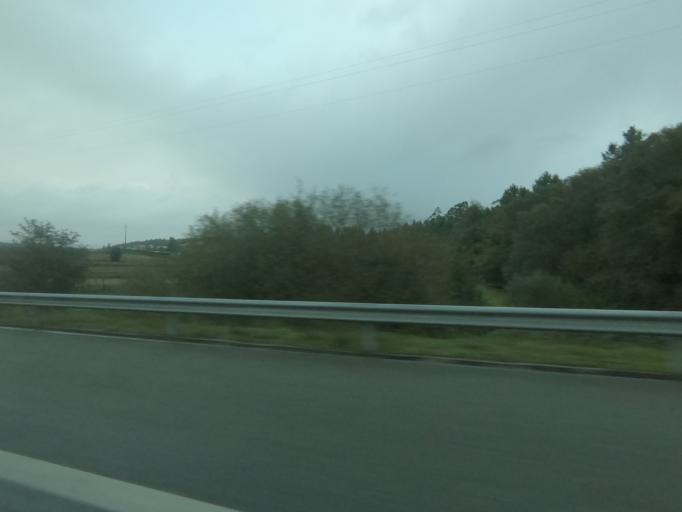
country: PT
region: Braga
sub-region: Barcelos
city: Galegos
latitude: 41.6125
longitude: -8.5508
